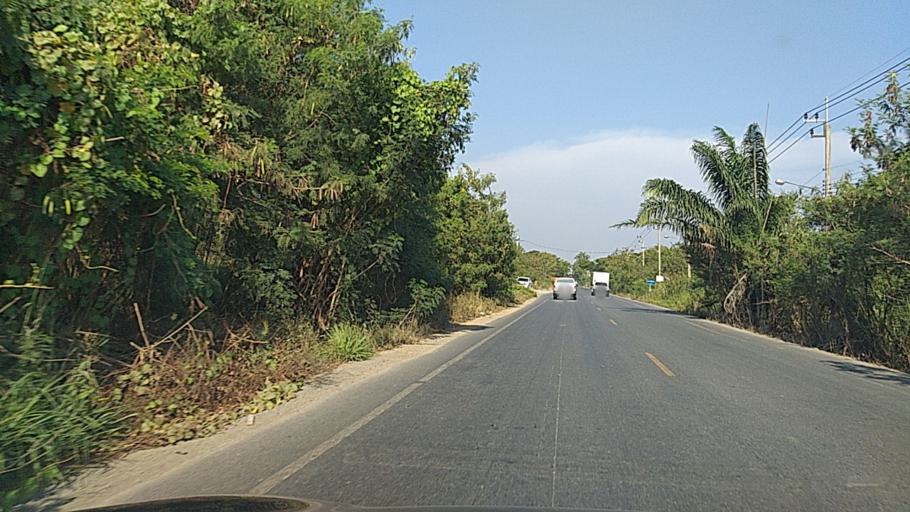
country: TH
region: Nonthaburi
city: Bang Yai
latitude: 13.8805
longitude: 100.3146
